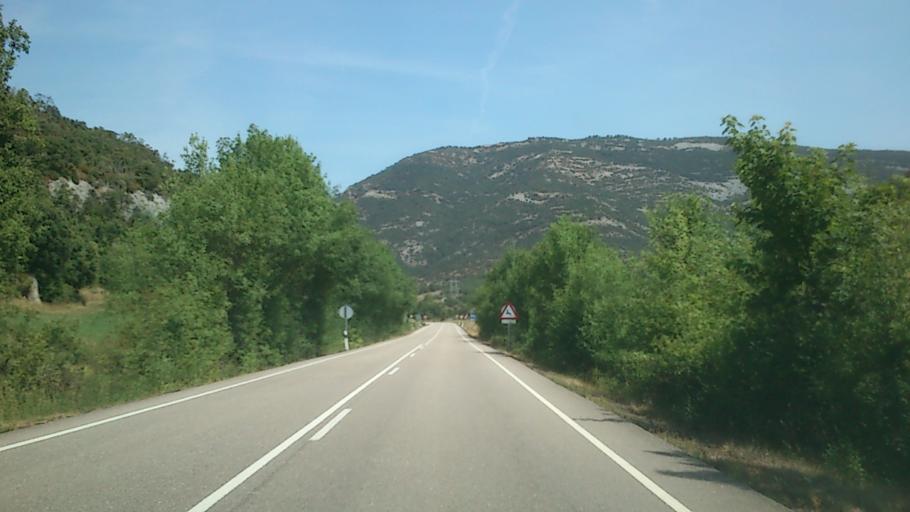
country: ES
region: Castille and Leon
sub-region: Provincia de Burgos
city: Trespaderne
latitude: 42.8772
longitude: -3.3287
